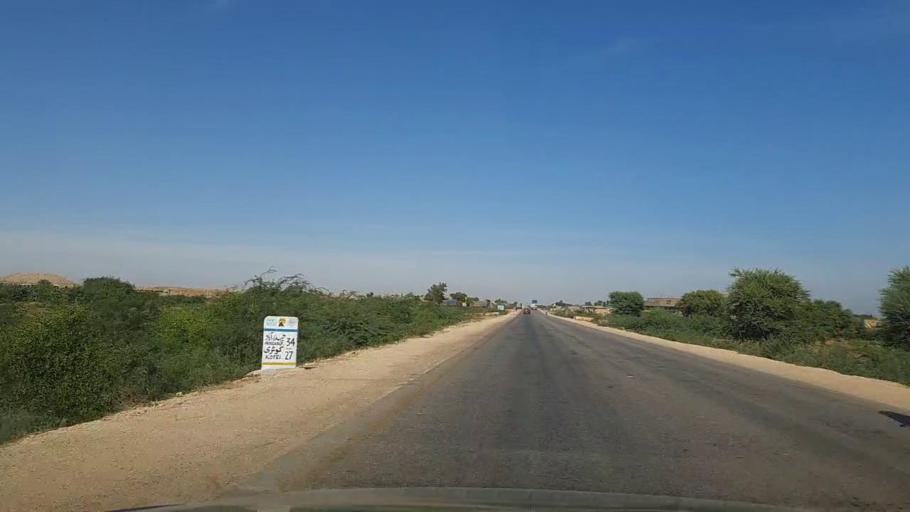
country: PK
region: Sindh
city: Kotri
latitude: 25.1782
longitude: 68.2398
